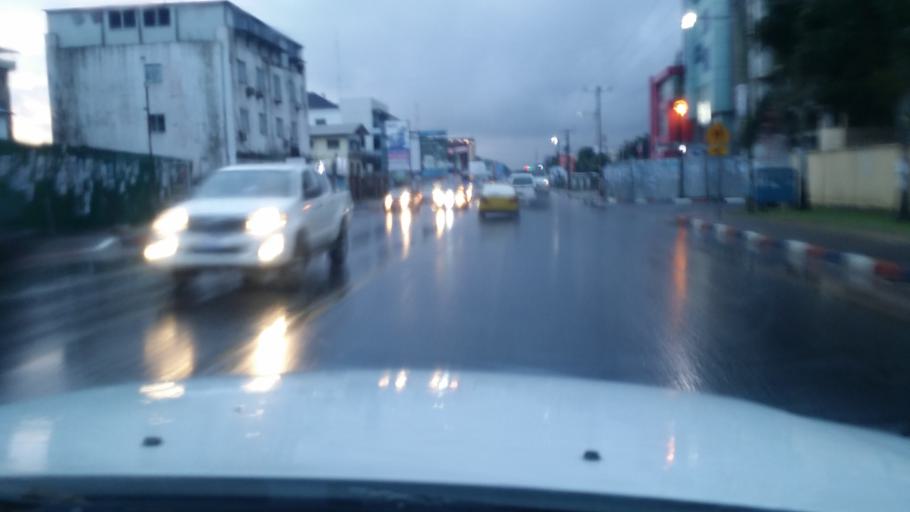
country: LR
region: Montserrado
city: Monrovia
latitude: 6.2937
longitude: -10.7844
